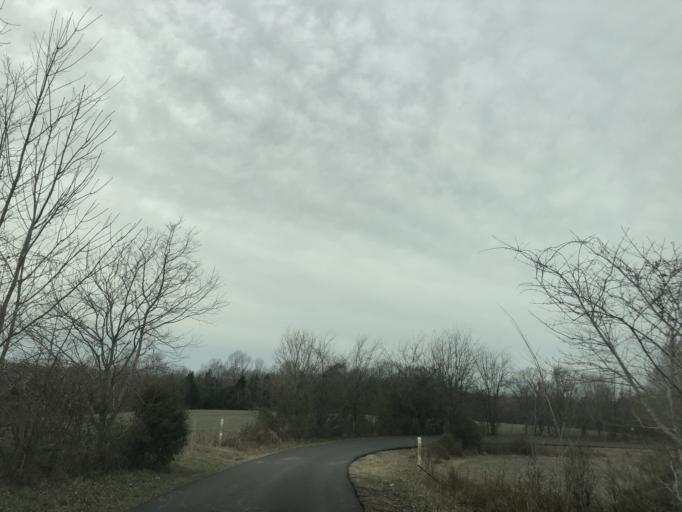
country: US
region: Tennessee
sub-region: Robertson County
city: Greenbrier
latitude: 36.4601
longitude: -86.7882
